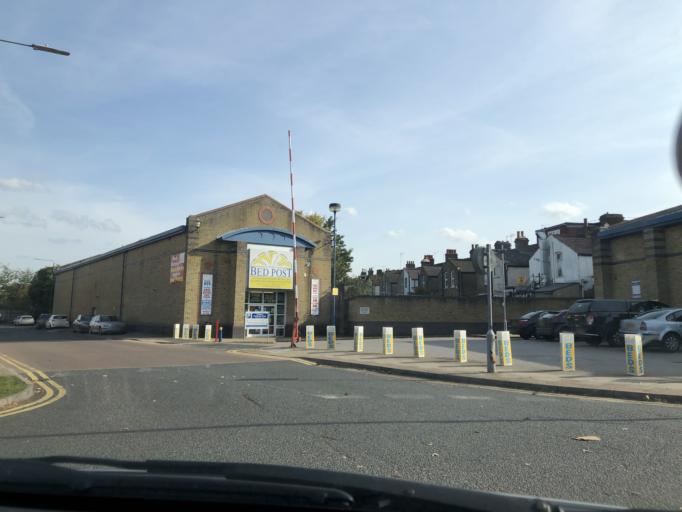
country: GB
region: England
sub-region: Greater London
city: Erith
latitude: 51.4506
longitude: 0.1822
